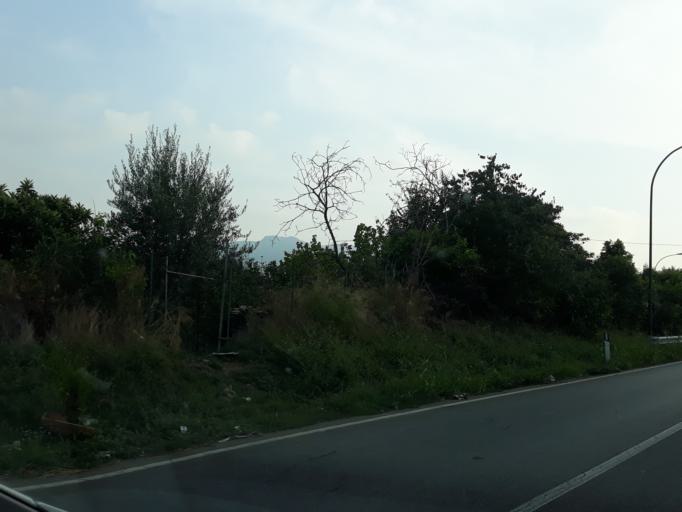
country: IT
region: Sicily
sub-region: Palermo
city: Monreale
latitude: 38.0827
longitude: 13.2999
